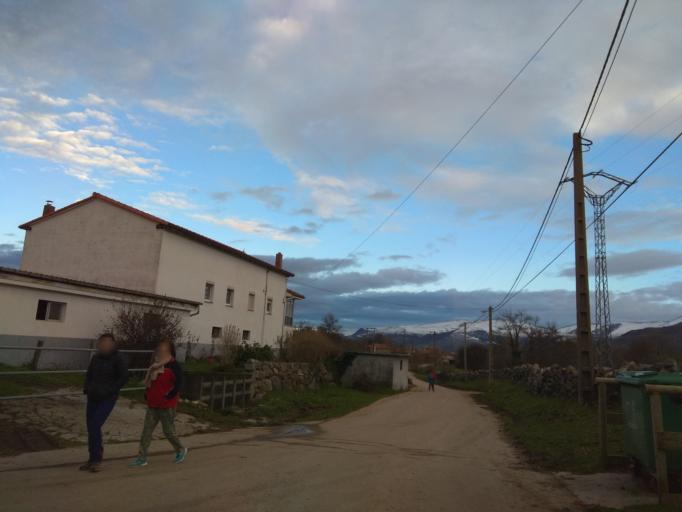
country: ES
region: Cantabria
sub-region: Provincia de Cantabria
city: Arredondo
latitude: 43.1977
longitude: -3.5731
